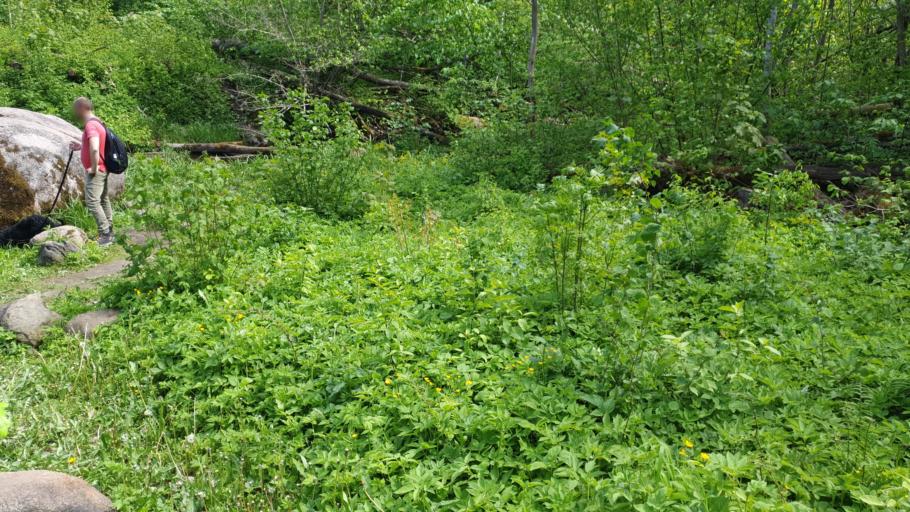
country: LT
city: Moletai
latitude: 55.0744
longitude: 25.4150
